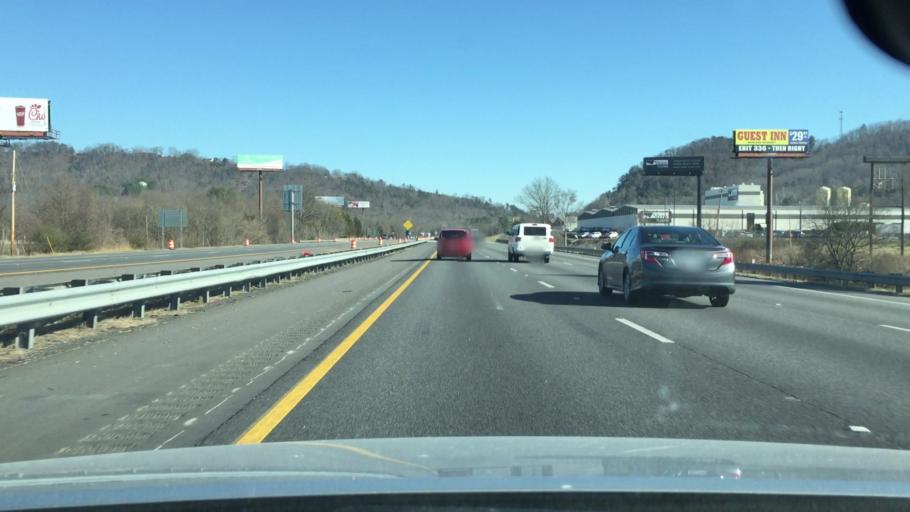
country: US
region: Georgia
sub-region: Catoosa County
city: Ringgold
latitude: 34.9089
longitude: -85.1175
